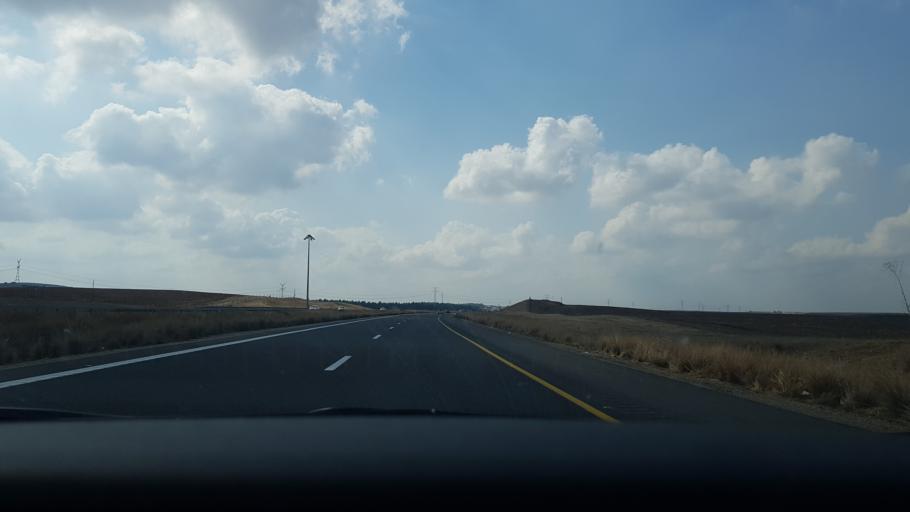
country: IL
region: Central District
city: Bene 'Ayish
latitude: 31.7068
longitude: 34.8195
